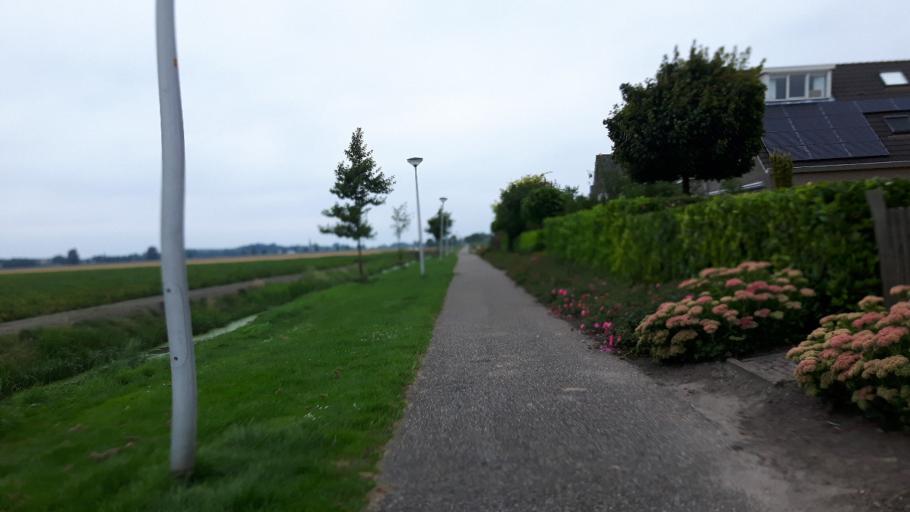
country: NL
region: South Holland
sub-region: Gemeente Nieuwkoop
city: Nieuwkoop
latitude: 52.1841
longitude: 4.7754
